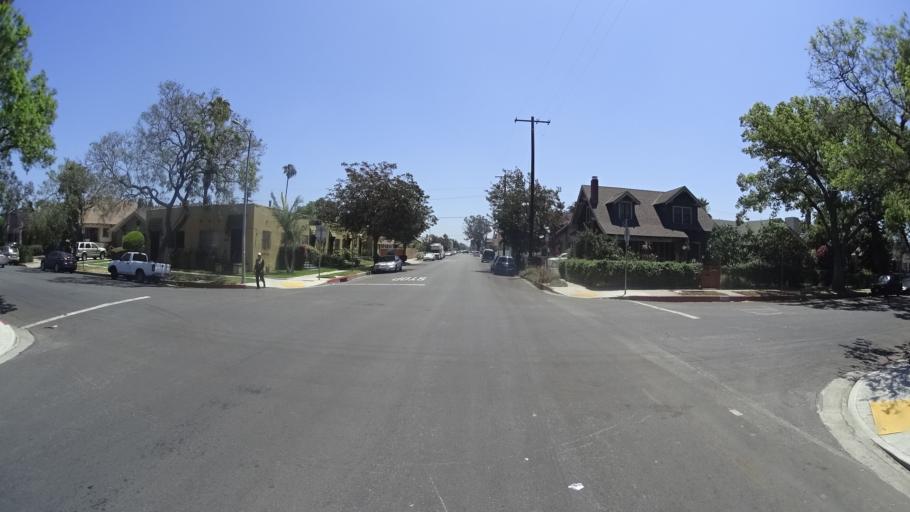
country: US
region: California
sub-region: Los Angeles County
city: View Park-Windsor Hills
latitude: 34.0291
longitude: -118.3080
